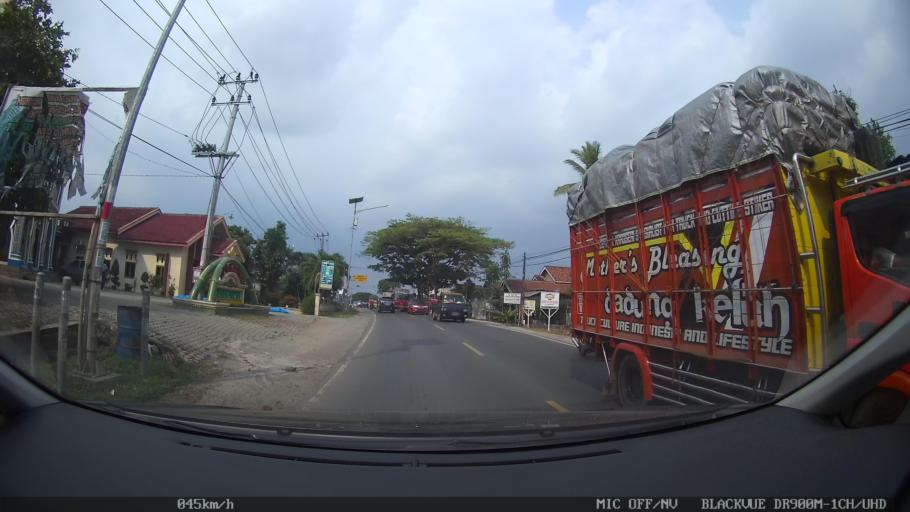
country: ID
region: Lampung
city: Gadingrejo
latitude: -5.3802
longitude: 105.0284
